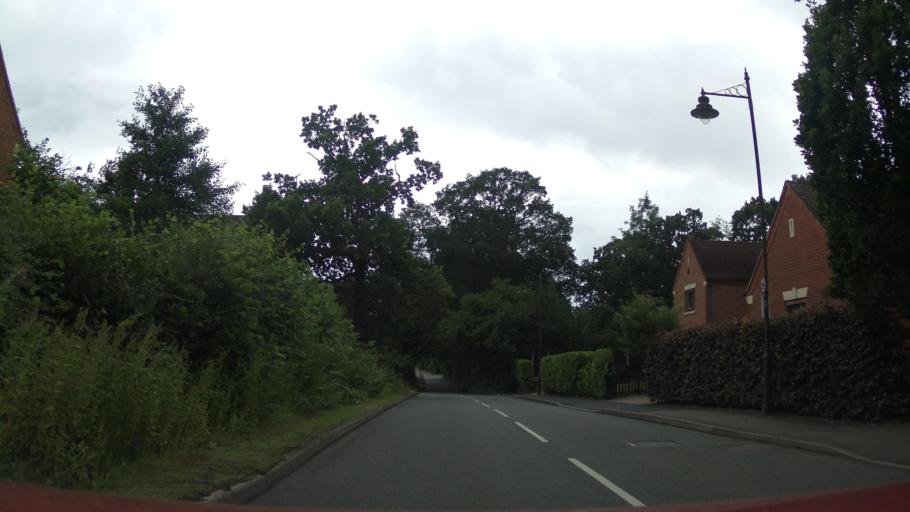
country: GB
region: England
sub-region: Solihull
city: Dickens Heath
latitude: 52.3835
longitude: -1.8398
